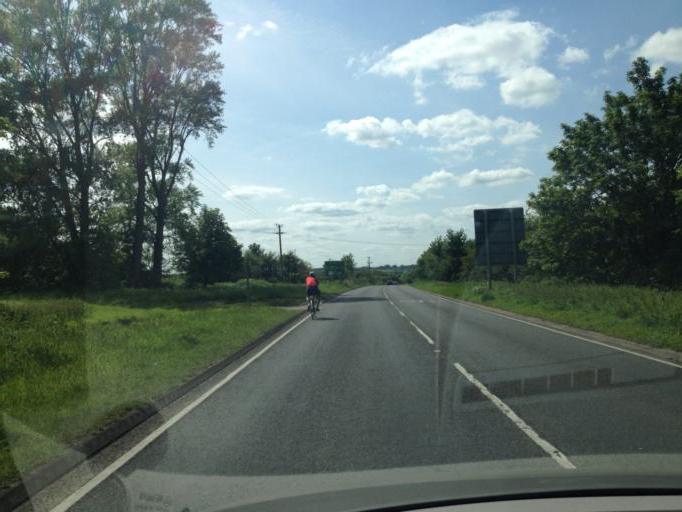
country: GB
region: England
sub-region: Oxfordshire
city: Wheatley
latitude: 51.7383
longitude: -1.0857
